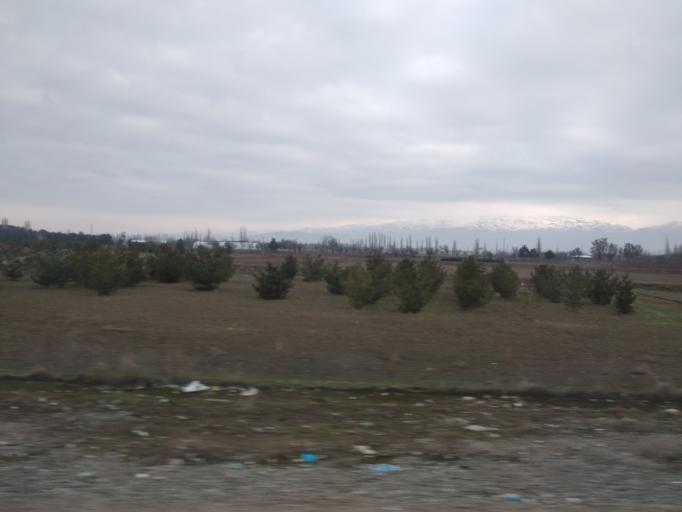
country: TR
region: Erzincan
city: Erzincan
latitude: 39.7203
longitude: 39.4867
